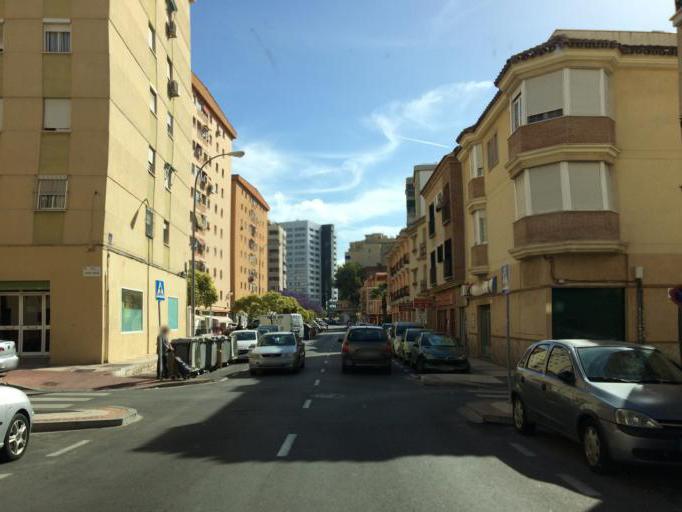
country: ES
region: Andalusia
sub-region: Provincia de Malaga
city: Malaga
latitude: 36.7138
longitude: -4.4383
